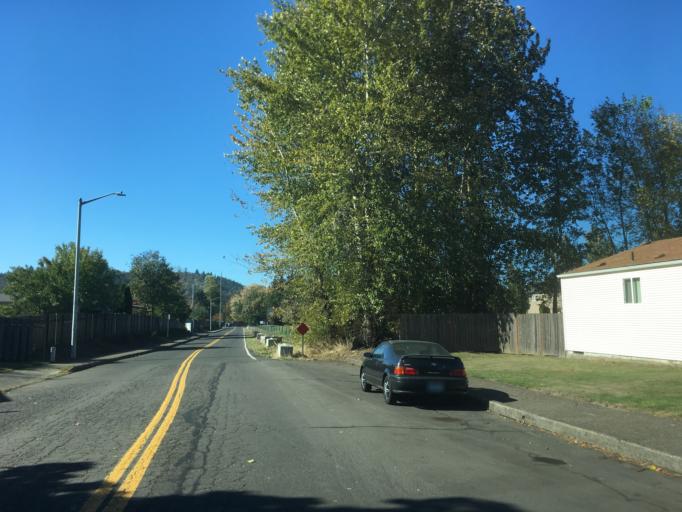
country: US
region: Oregon
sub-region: Multnomah County
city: Gresham
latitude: 45.4904
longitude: -122.4108
